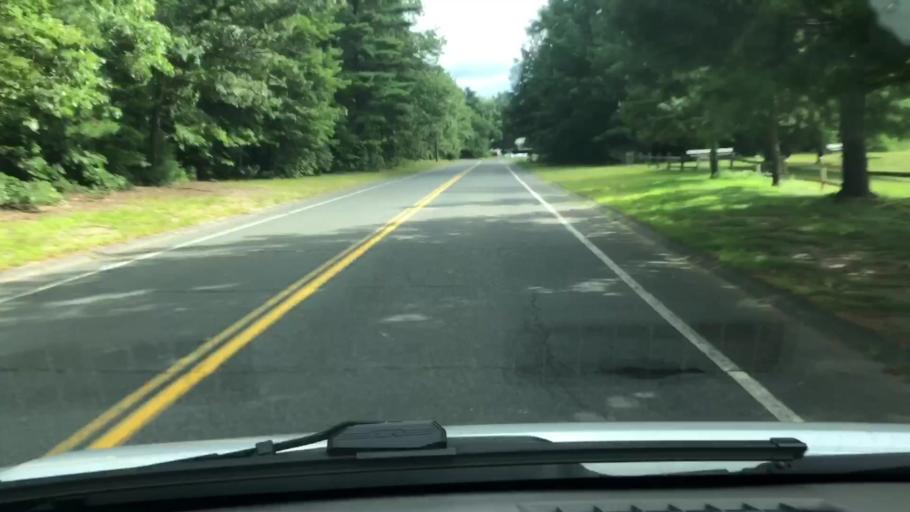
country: US
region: Massachusetts
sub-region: Franklin County
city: Turners Falls
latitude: 42.5989
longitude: -72.5239
